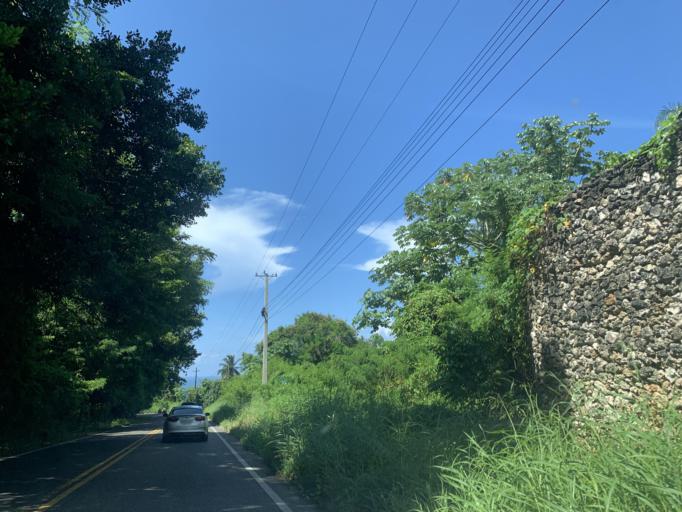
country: DO
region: Maria Trinidad Sanchez
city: Cabrera
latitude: 19.6534
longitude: -69.9338
